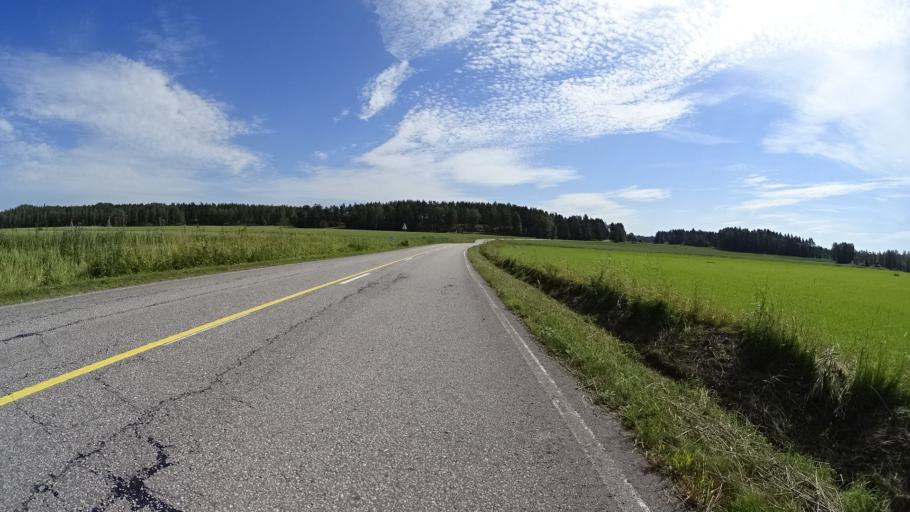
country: FI
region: Uusimaa
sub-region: Helsinki
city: Kirkkonummi
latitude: 60.1008
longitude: 24.4886
